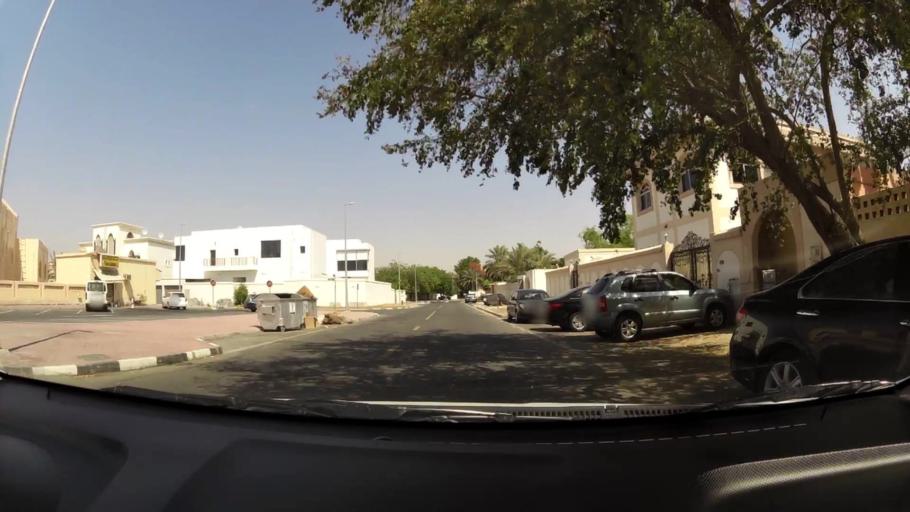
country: AE
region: Ash Shariqah
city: Sharjah
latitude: 25.2675
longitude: 55.3661
